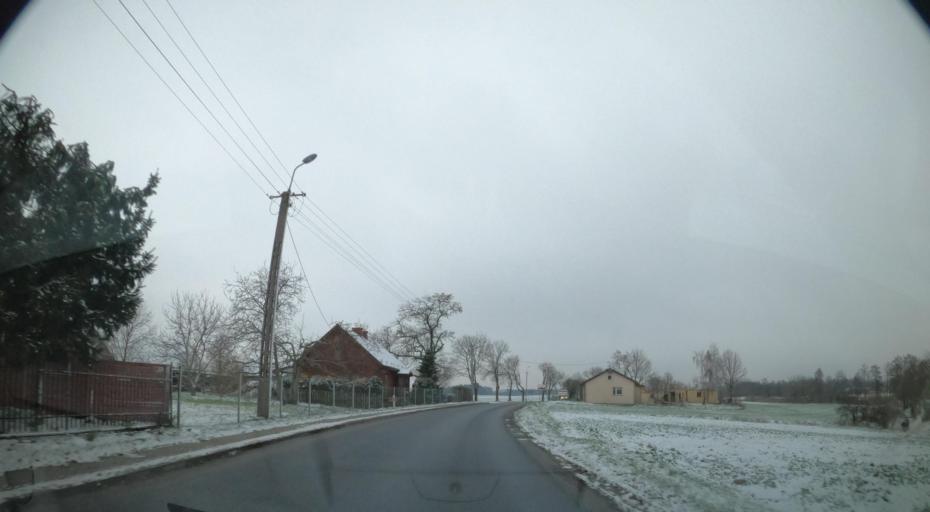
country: PL
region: Kujawsko-Pomorskie
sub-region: Powiat lipnowski
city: Wielgie
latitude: 52.6917
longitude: 19.2792
